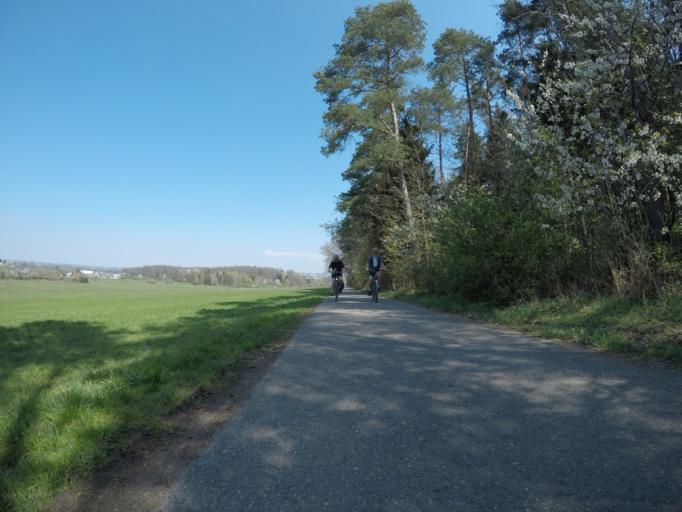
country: DE
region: Baden-Wuerttemberg
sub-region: Tuebingen Region
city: Wannweil
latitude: 48.4827
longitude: 9.1583
